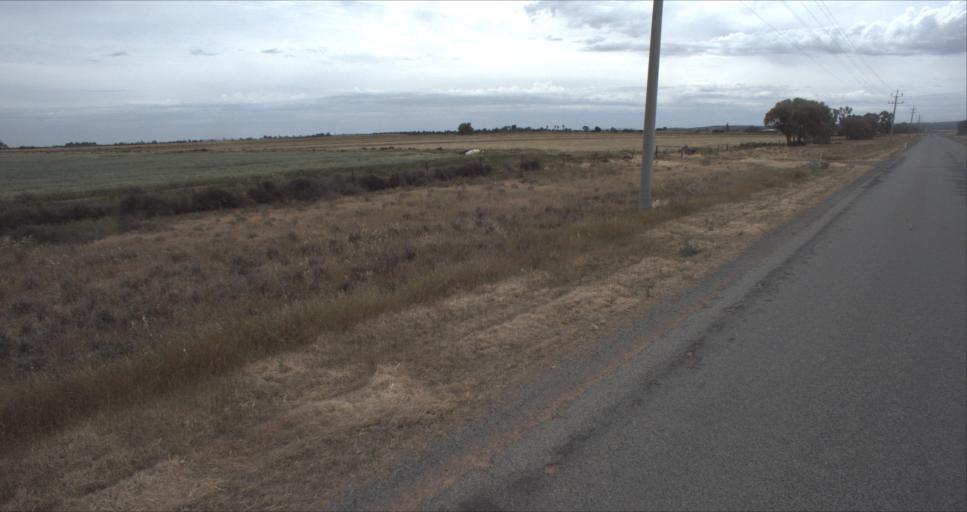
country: AU
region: New South Wales
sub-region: Leeton
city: Leeton
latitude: -34.4983
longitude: 146.4001
